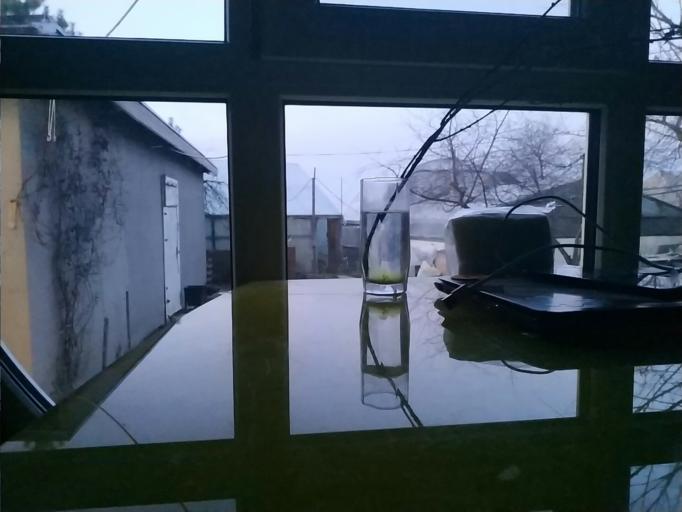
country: RU
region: Republic of Karelia
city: Sukkozero
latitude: 62.7697
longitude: 31.8578
